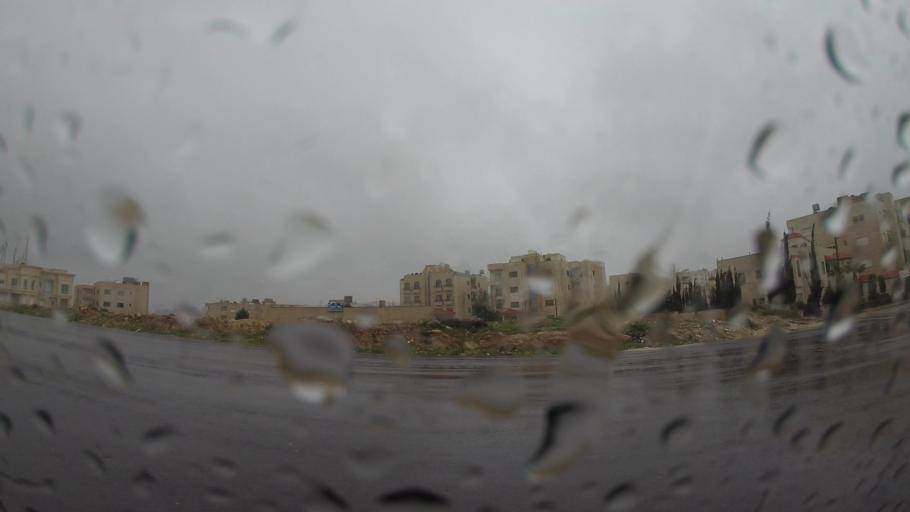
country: JO
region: Amman
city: Al Jubayhah
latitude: 32.0143
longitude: 35.8947
